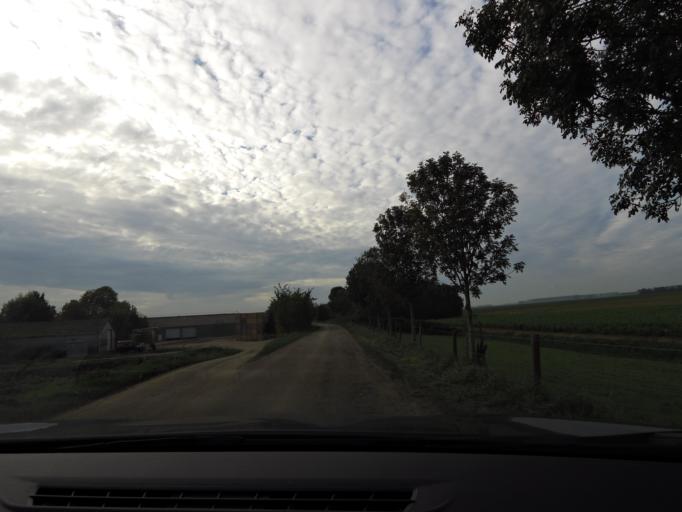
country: NL
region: South Holland
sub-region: Gemeente Goeree-Overflakkee
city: Middelharnis
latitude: 51.7185
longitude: 4.2021
